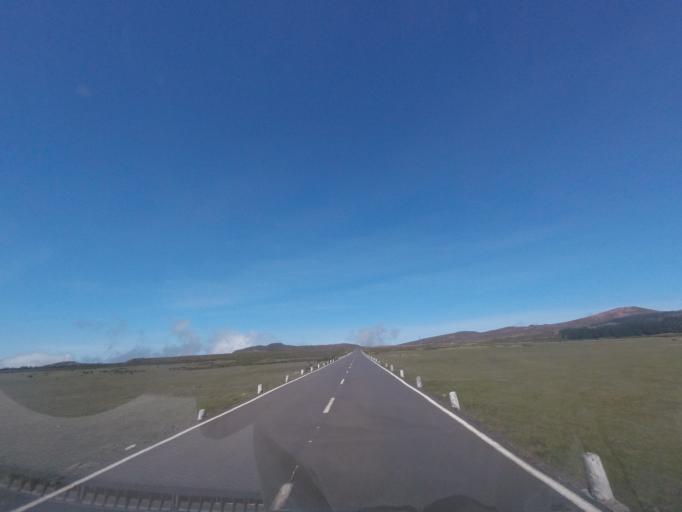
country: PT
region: Madeira
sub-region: Calheta
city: Arco da Calheta
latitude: 32.7488
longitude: -17.0982
